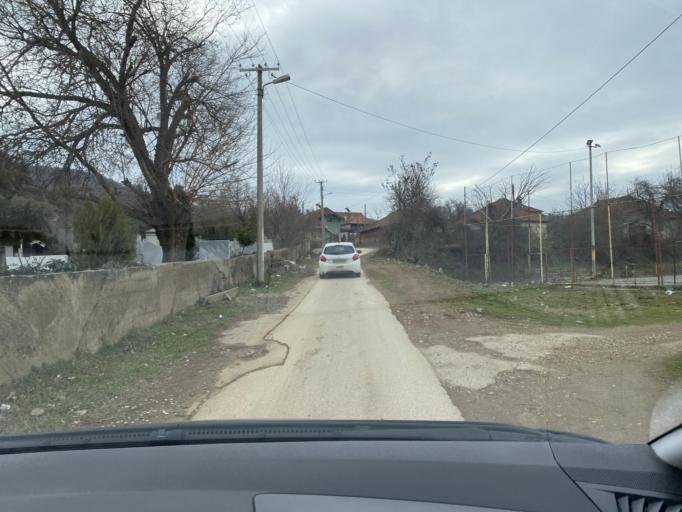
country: MK
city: Radishani
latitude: 42.1068
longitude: 21.4562
